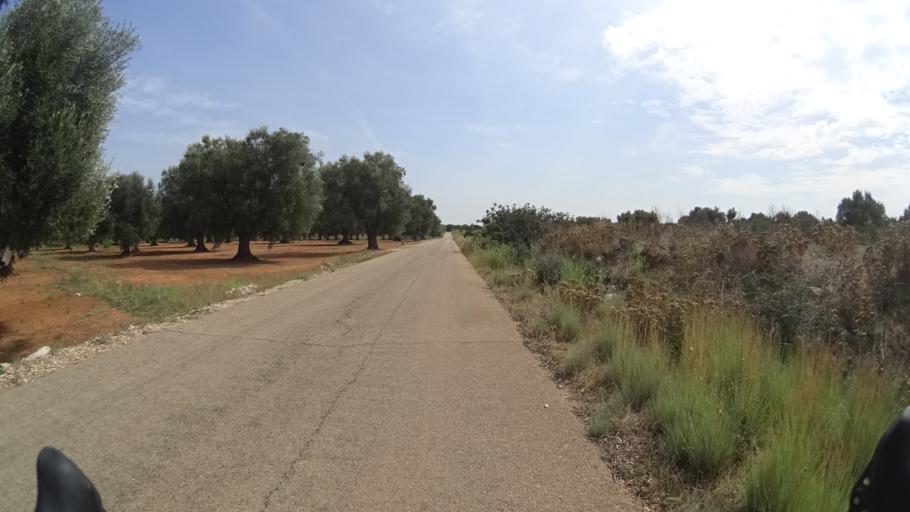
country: IT
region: Apulia
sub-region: Provincia di Lecce
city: Porto Cesareo
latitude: 40.3225
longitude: 17.8958
